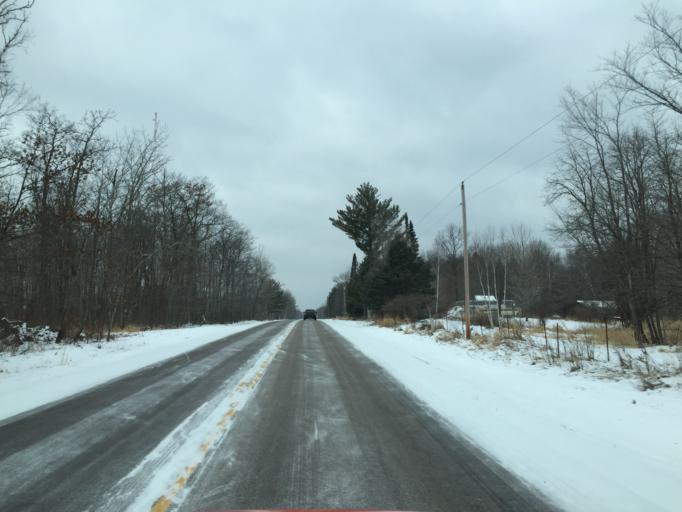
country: US
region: Minnesota
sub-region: Mille Lacs County
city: Vineland
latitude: 46.0776
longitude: -93.7598
